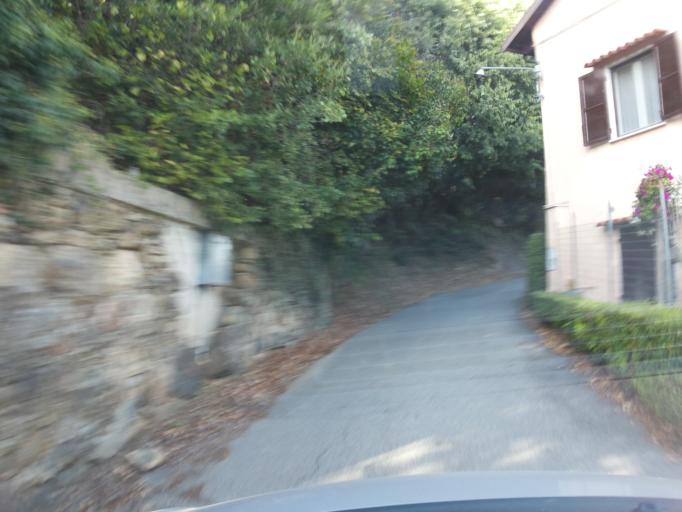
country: IT
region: Piedmont
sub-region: Provincia di Biella
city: Dorzano
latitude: 45.4388
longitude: 8.0915
